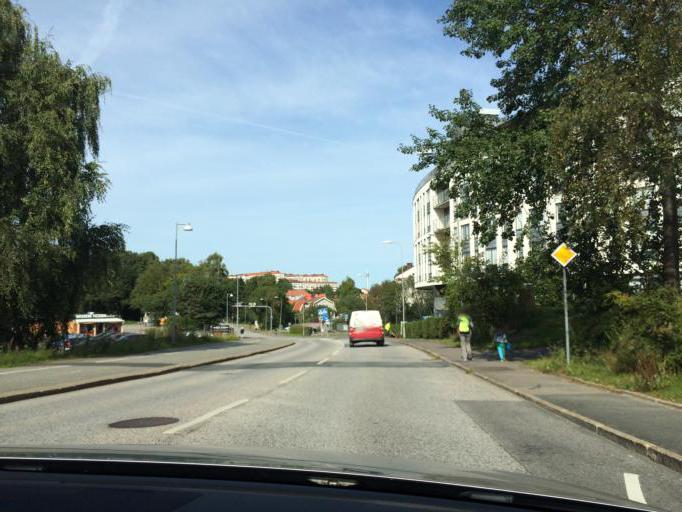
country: SE
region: Vaestra Goetaland
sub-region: Goteborg
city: Goeteborg
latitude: 57.6816
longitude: 11.9844
